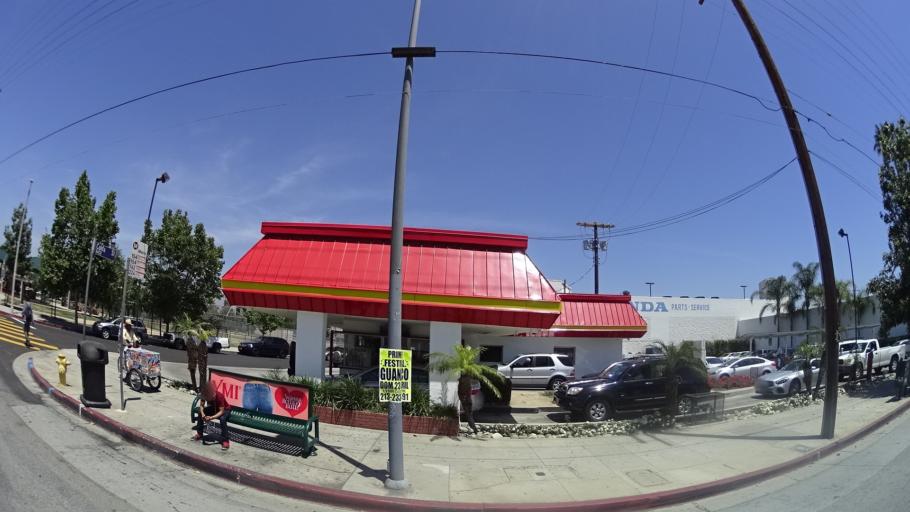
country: US
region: California
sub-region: Los Angeles County
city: North Hollywood
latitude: 34.1774
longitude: -118.3821
